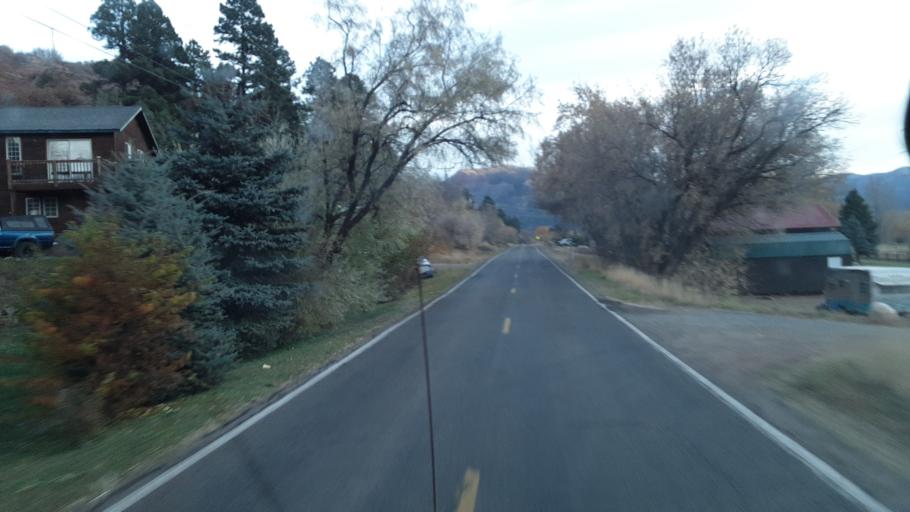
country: US
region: Colorado
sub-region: La Plata County
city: Durango
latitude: 37.3814
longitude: -107.8523
